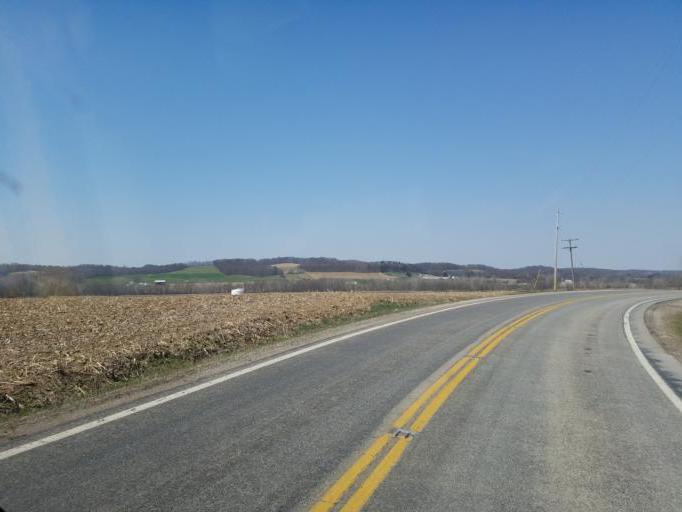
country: US
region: Ohio
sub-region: Ashland County
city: Loudonville
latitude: 40.6878
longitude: -82.1450
